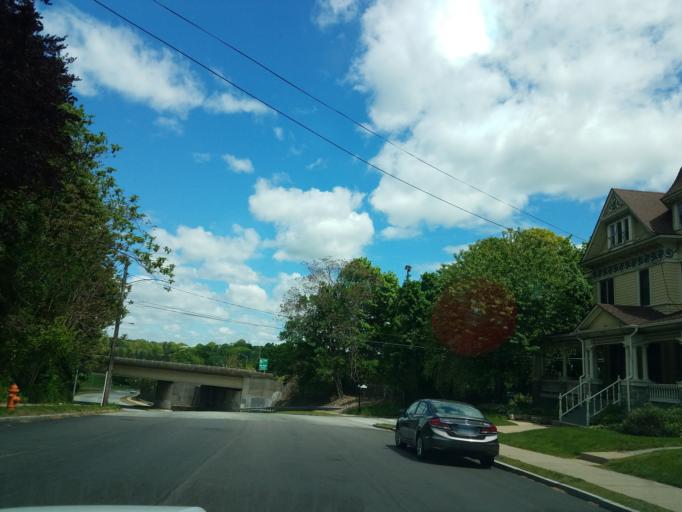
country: US
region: Connecticut
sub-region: New London County
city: New London
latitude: 41.3610
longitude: -72.1030
